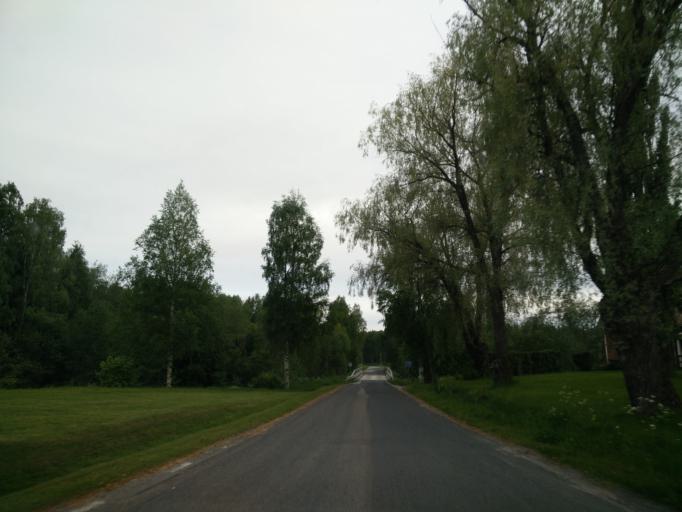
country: SE
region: Vaesternorrland
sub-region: Kramfors Kommun
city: Kramfors
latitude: 63.0482
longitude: 17.8008
